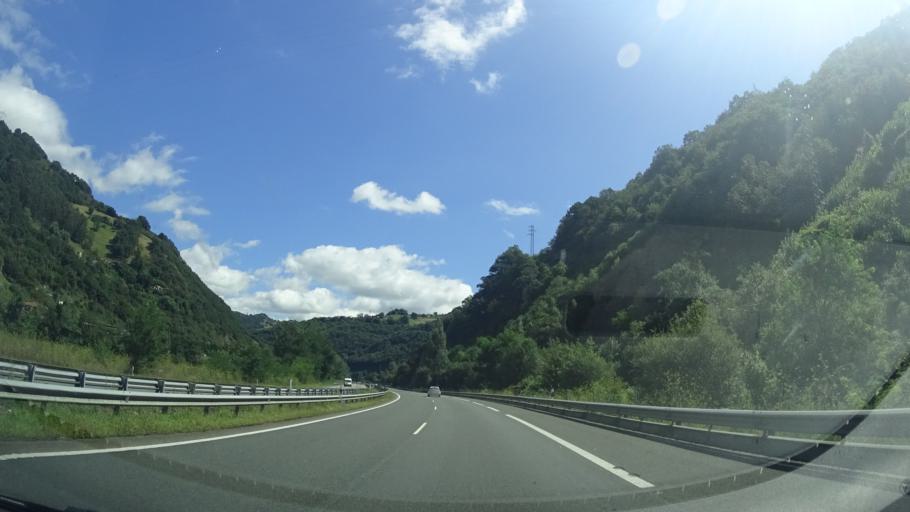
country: ES
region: Asturias
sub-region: Province of Asturias
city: Pola de Lena
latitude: 43.1846
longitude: -5.8018
